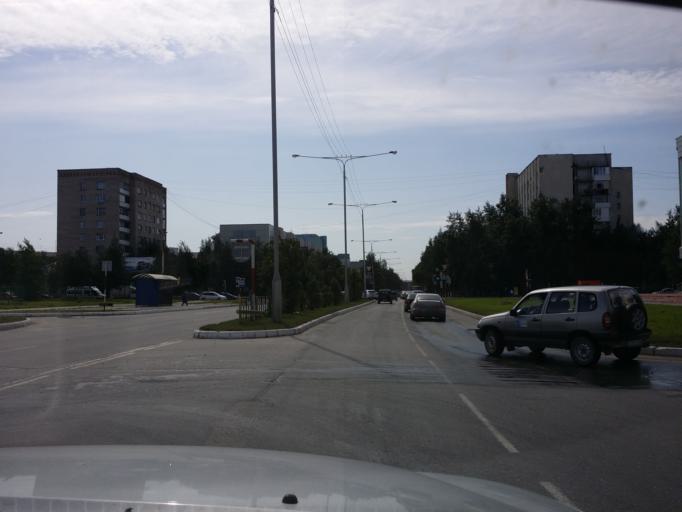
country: RU
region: Khanty-Mansiyskiy Avtonomnyy Okrug
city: Nizhnevartovsk
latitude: 60.9464
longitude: 76.5660
